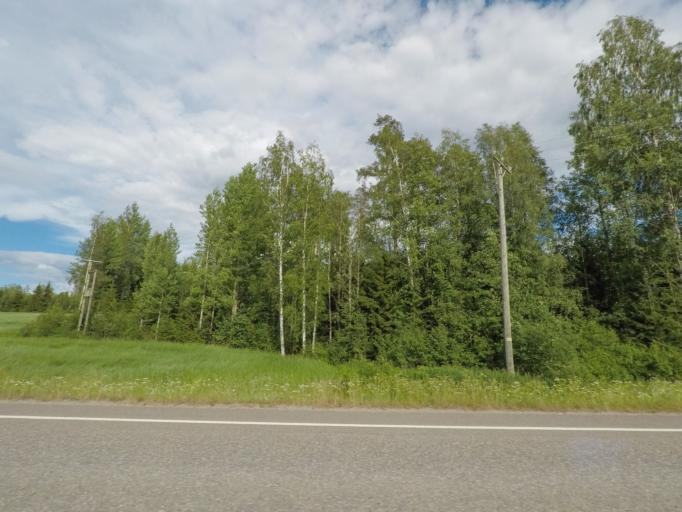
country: FI
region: Uusimaa
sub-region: Porvoo
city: Pukkila
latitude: 60.8113
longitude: 25.4815
